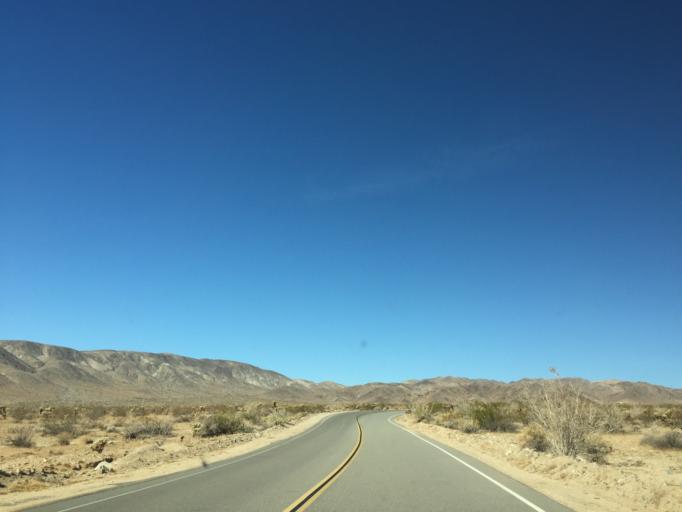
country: US
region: California
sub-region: San Bernardino County
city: Twentynine Palms
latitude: 33.9238
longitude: -115.9206
